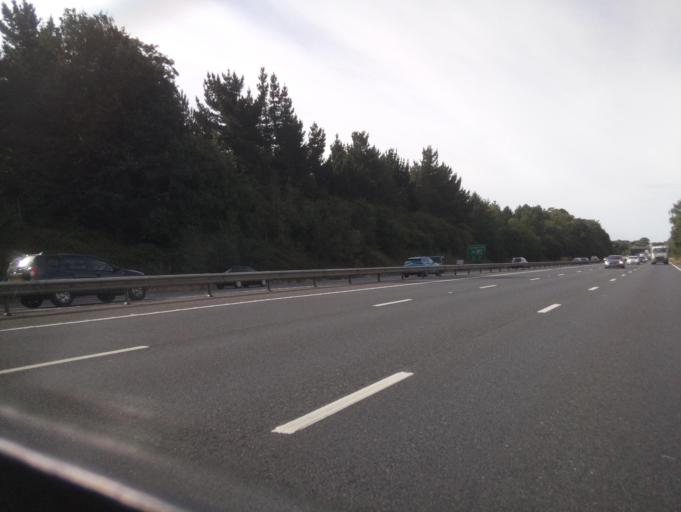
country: GB
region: England
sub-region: Surrey
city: Ripley
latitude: 51.3017
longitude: -0.4824
